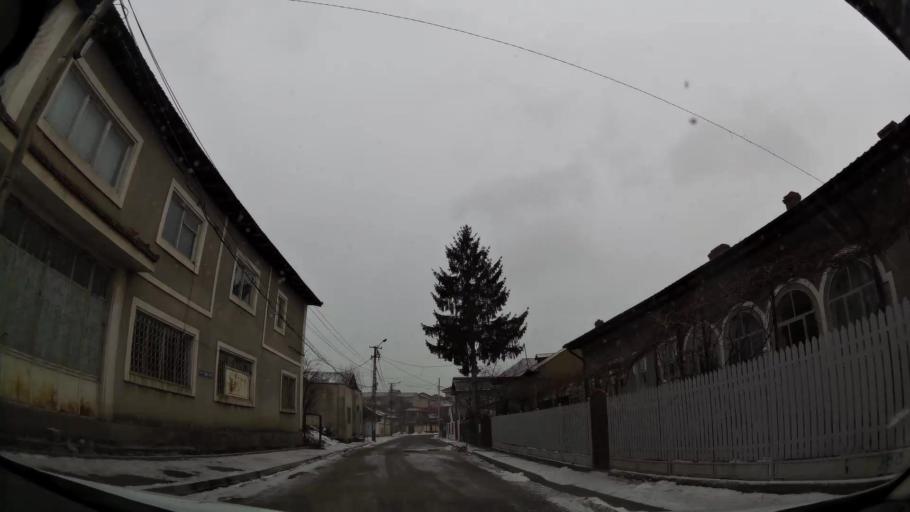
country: RO
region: Dambovita
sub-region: Municipiul Targoviste
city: Targoviste
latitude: 44.9358
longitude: 25.4497
